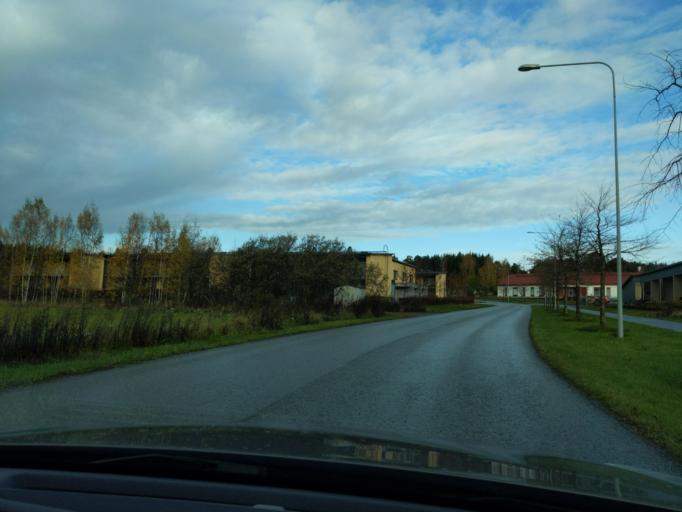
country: FI
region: Varsinais-Suomi
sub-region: Turku
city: Raisio
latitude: 60.4726
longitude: 22.1369
